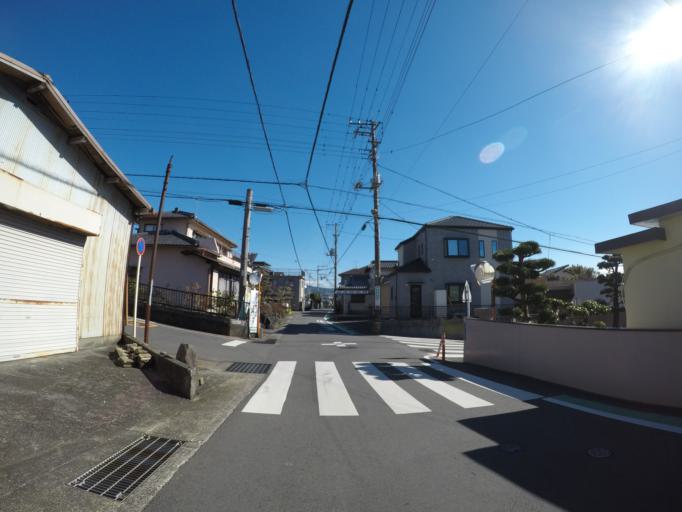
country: JP
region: Shizuoka
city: Fuji
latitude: 35.1671
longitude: 138.6940
